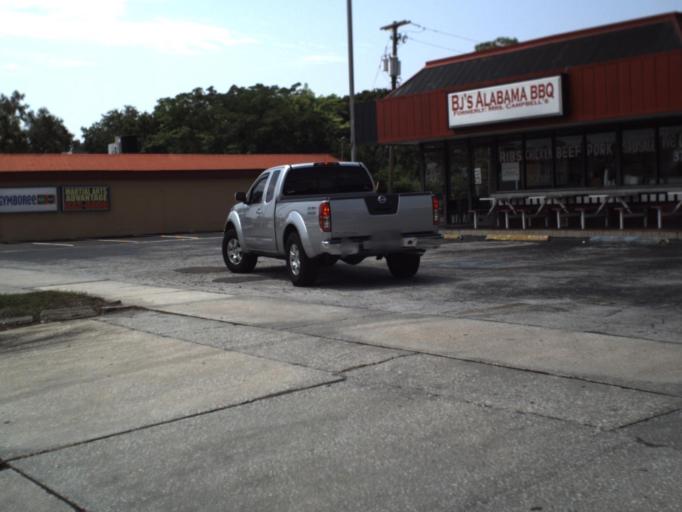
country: US
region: Florida
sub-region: Hillsborough County
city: Tampa
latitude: 27.9152
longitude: -82.5061
